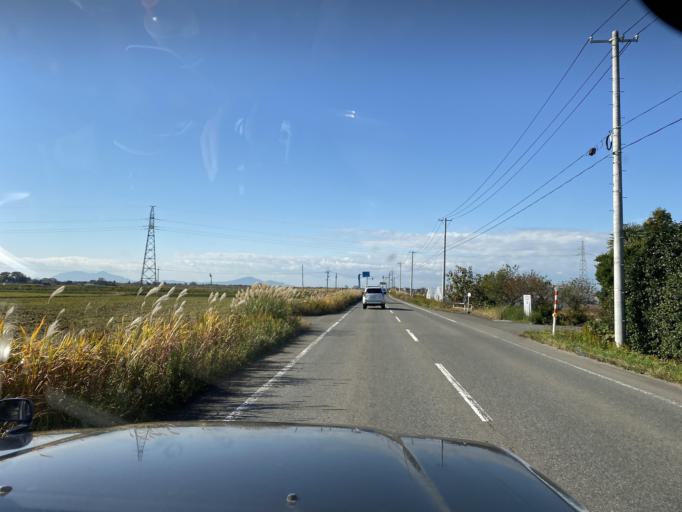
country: JP
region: Niigata
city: Niitsu-honcho
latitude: 37.8163
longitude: 139.0804
